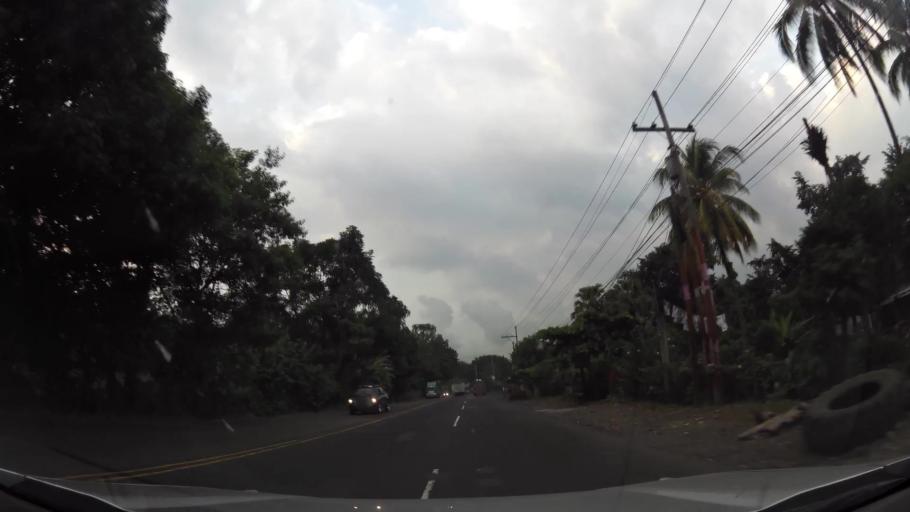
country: GT
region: Escuintla
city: Siquinala
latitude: 14.2911
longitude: -90.9407
